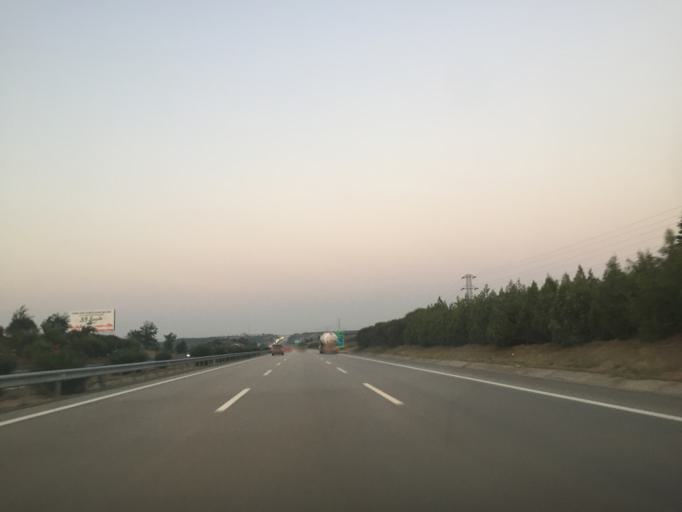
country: TR
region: Bursa
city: Gorukle
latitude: 40.2570
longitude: 28.8255
